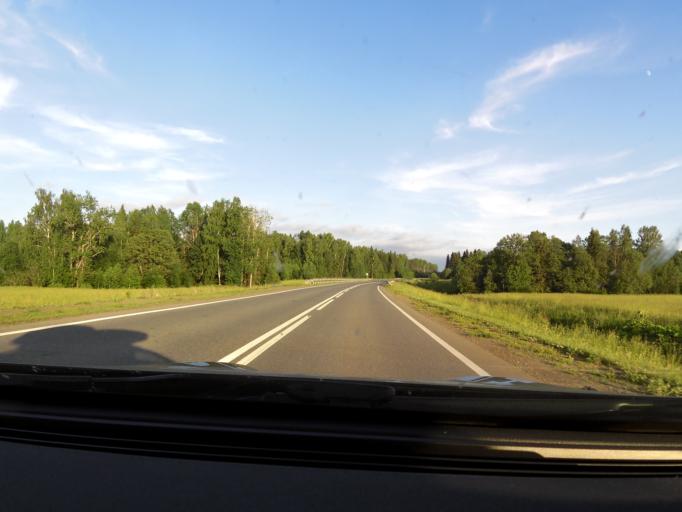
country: RU
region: Perm
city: Siva
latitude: 58.5055
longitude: 54.0404
